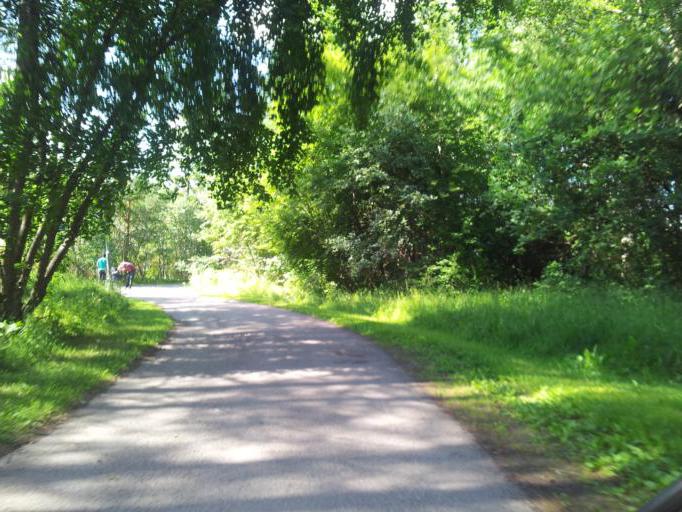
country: SE
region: Uppsala
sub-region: Uppsala Kommun
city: Uppsala
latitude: 59.8784
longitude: 17.6610
